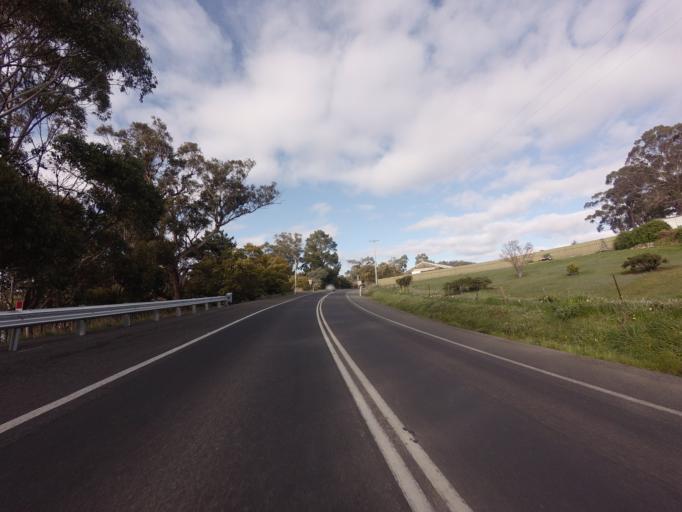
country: AU
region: Tasmania
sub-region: Huon Valley
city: Geeveston
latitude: -43.1570
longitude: 146.9801
